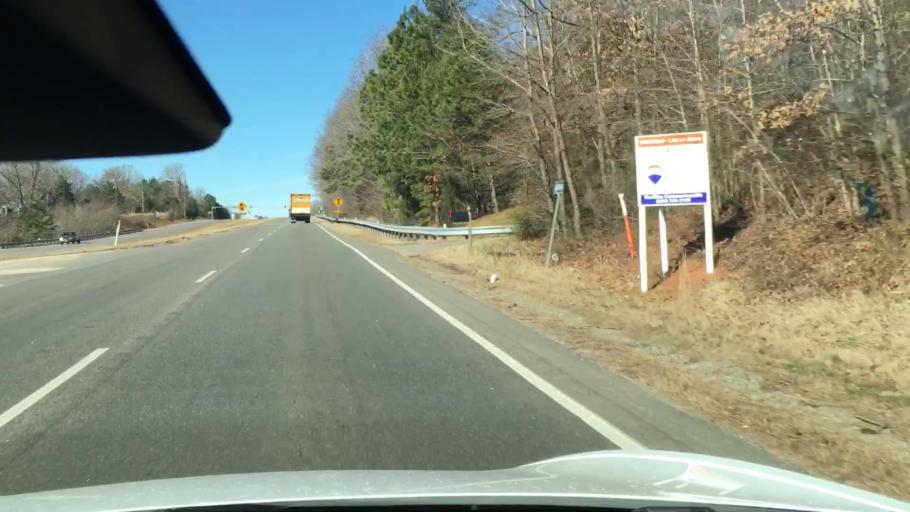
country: US
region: Virginia
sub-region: Powhatan County
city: Powhatan
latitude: 37.5163
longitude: -77.8011
